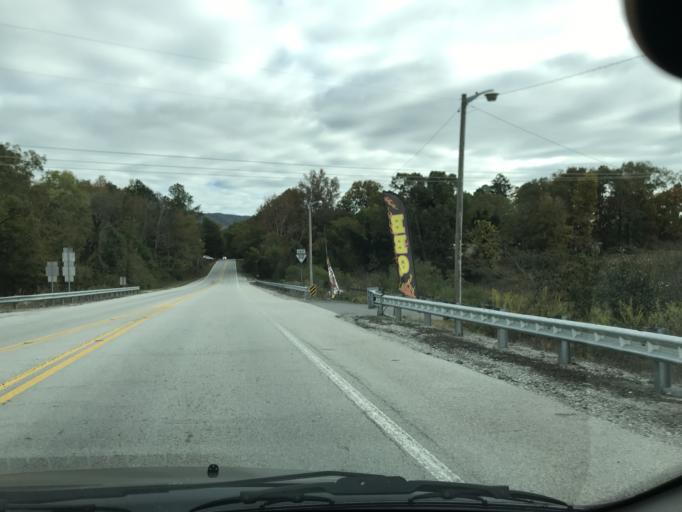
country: US
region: Tennessee
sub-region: Hamilton County
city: Lakesite
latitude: 35.1851
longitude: -85.0591
